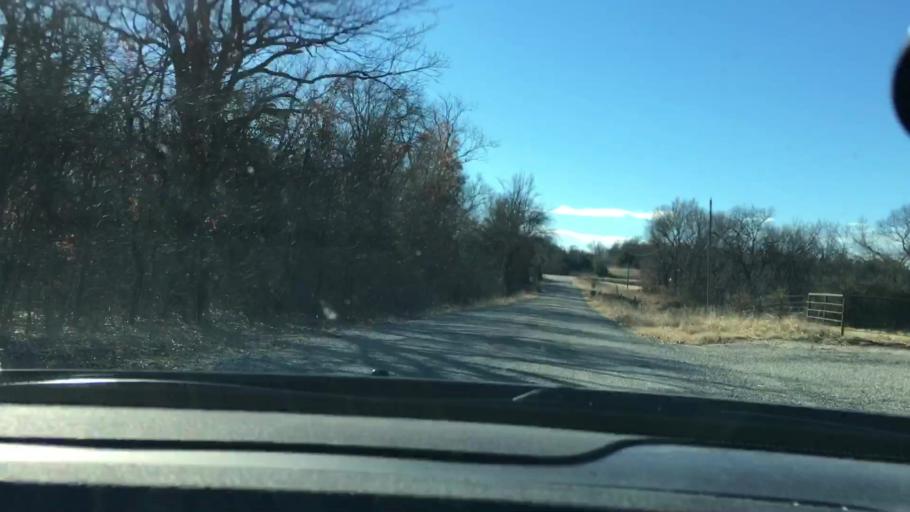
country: US
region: Oklahoma
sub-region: Johnston County
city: Tishomingo
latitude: 34.1170
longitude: -96.6361
